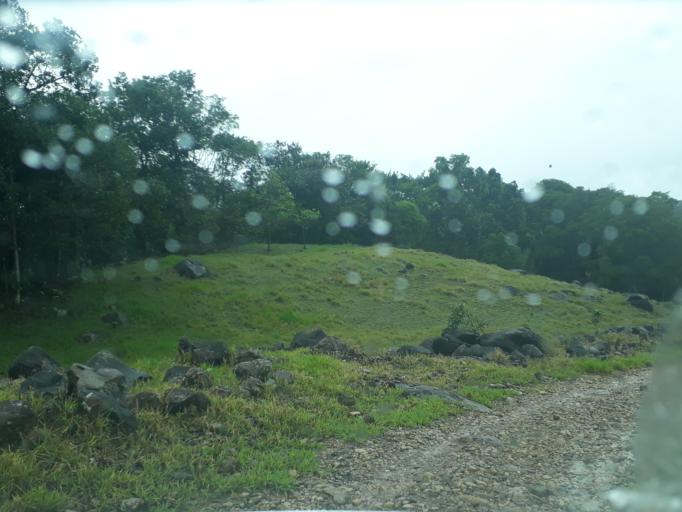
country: CO
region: Cundinamarca
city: Medina
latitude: 4.5307
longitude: -73.3683
